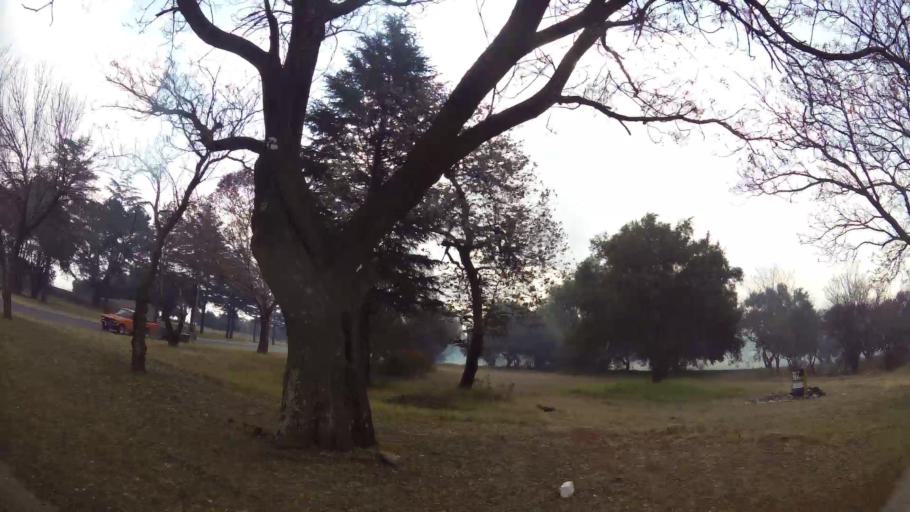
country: ZA
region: Mpumalanga
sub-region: Nkangala District Municipality
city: Delmas
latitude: -26.1451
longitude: 28.6714
